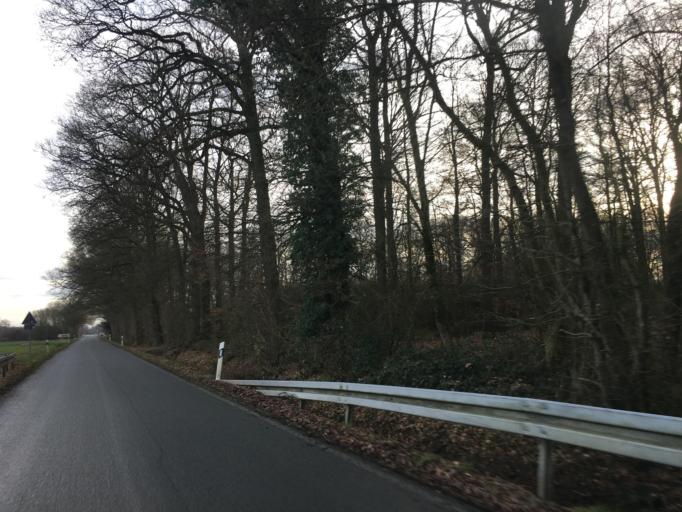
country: DE
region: North Rhine-Westphalia
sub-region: Regierungsbezirk Munster
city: Dulmen
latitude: 51.8269
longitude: 7.3560
